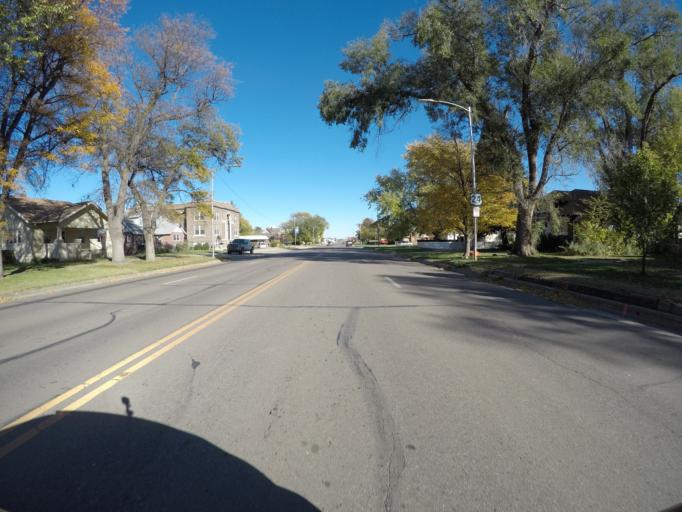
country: US
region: Kansas
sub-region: Thomas County
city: Colby
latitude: 39.3970
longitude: -101.0516
